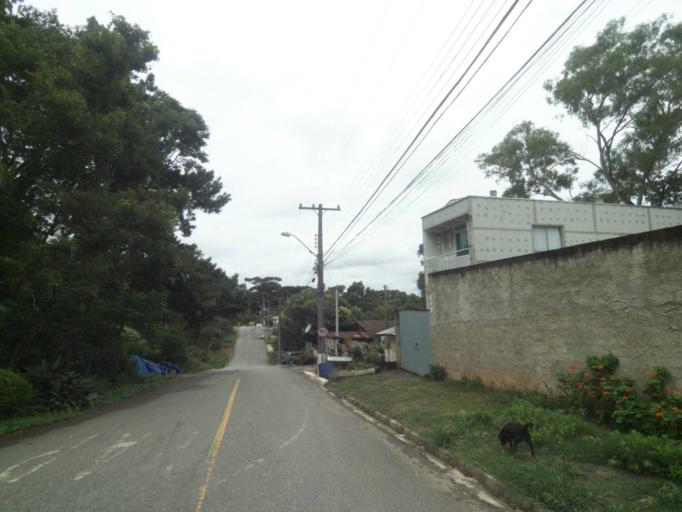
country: BR
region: Parana
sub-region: Curitiba
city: Curitiba
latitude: -25.4450
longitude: -49.3297
